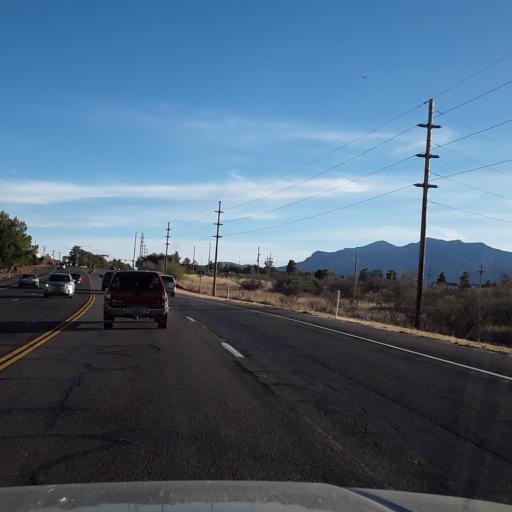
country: US
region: Arizona
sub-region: Cochise County
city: Sierra Vista
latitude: 31.5573
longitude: -110.3085
